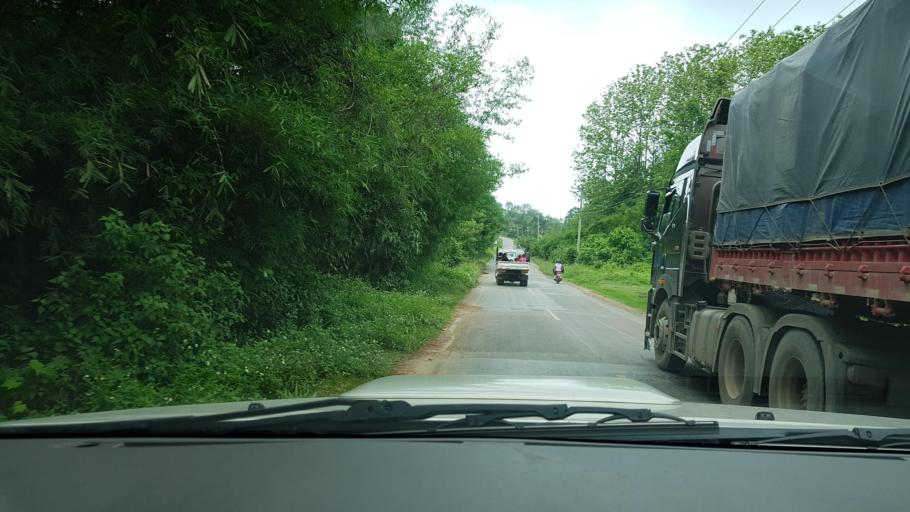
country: LA
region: Loungnamtha
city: Muang Nale
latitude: 20.3140
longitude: 101.6536
